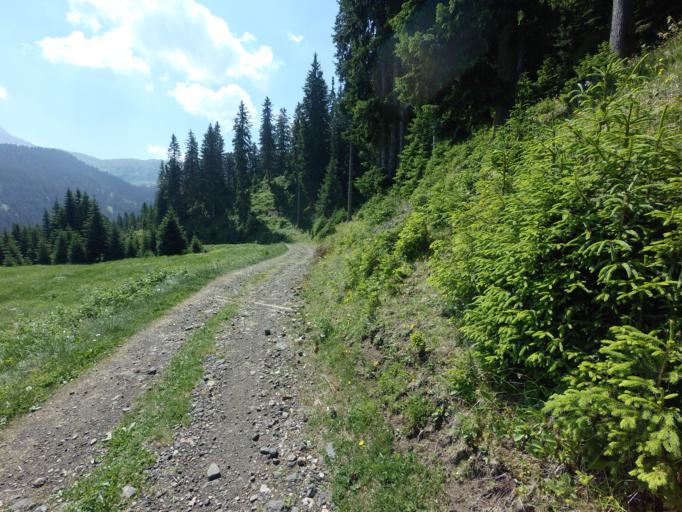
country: IT
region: Trentino-Alto Adige
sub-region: Bolzano
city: Ortisei
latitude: 46.5216
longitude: 11.6595
